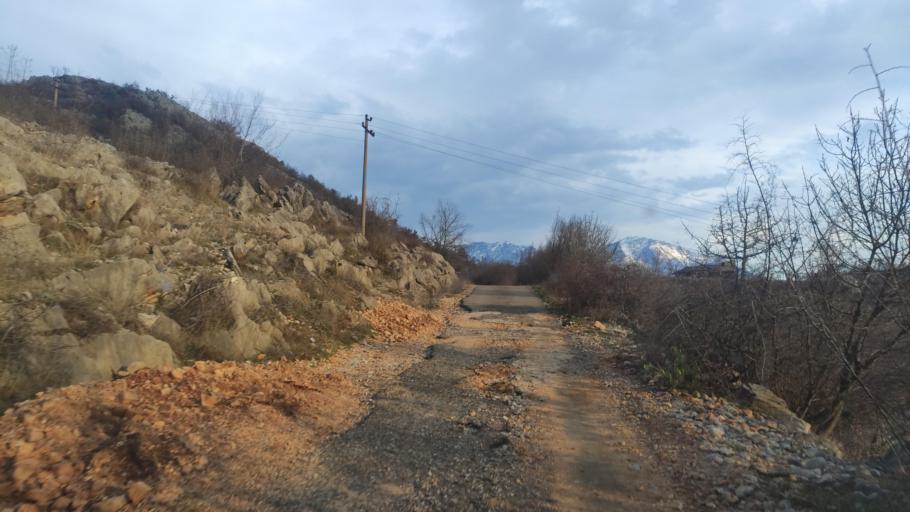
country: AL
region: Shkoder
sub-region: Rrethi i Malesia e Madhe
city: Gruemire
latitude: 42.2389
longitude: 19.5359
